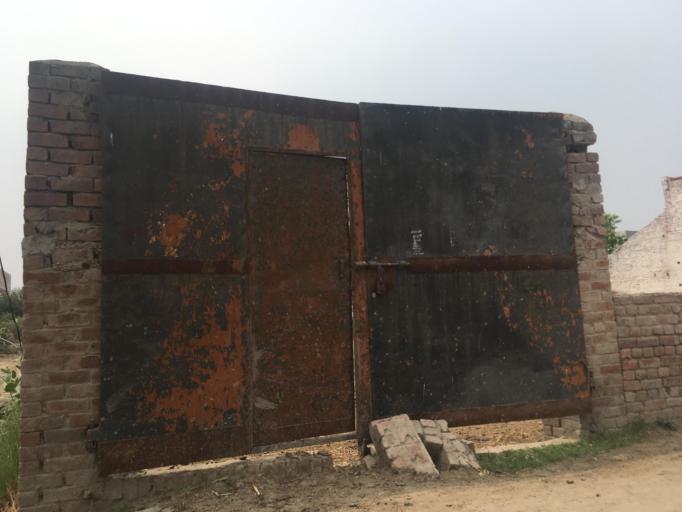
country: PK
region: Punjab
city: Lahore
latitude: 31.6218
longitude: 74.3468
